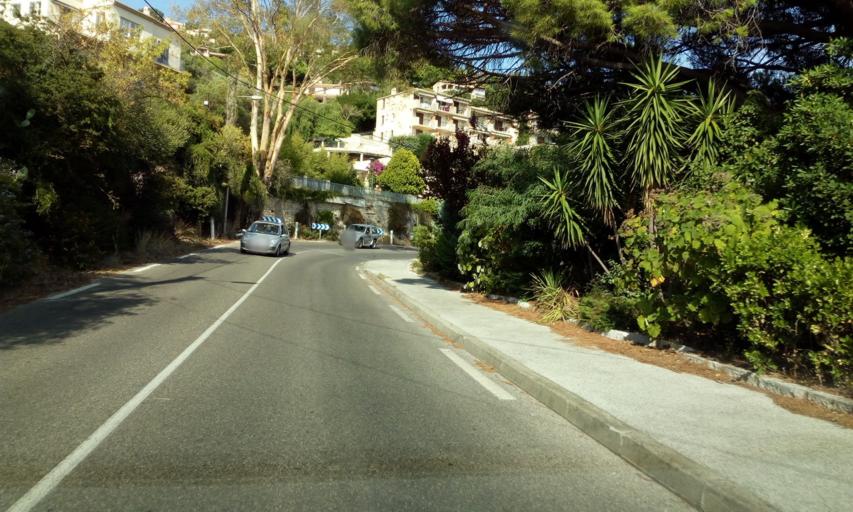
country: FR
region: Provence-Alpes-Cote d'Azur
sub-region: Departement du Var
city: Le Lavandou
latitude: 43.1450
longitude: 6.3860
